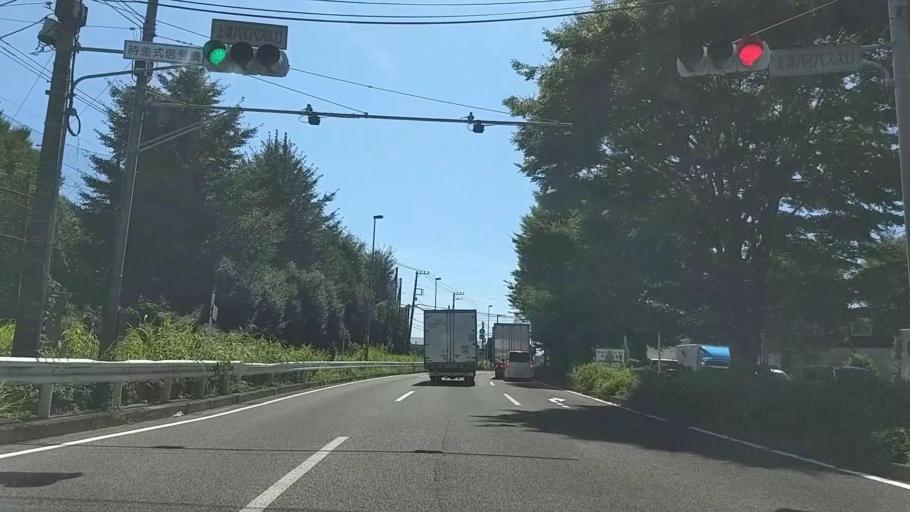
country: JP
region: Kanagawa
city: Zama
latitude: 35.5416
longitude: 139.3608
